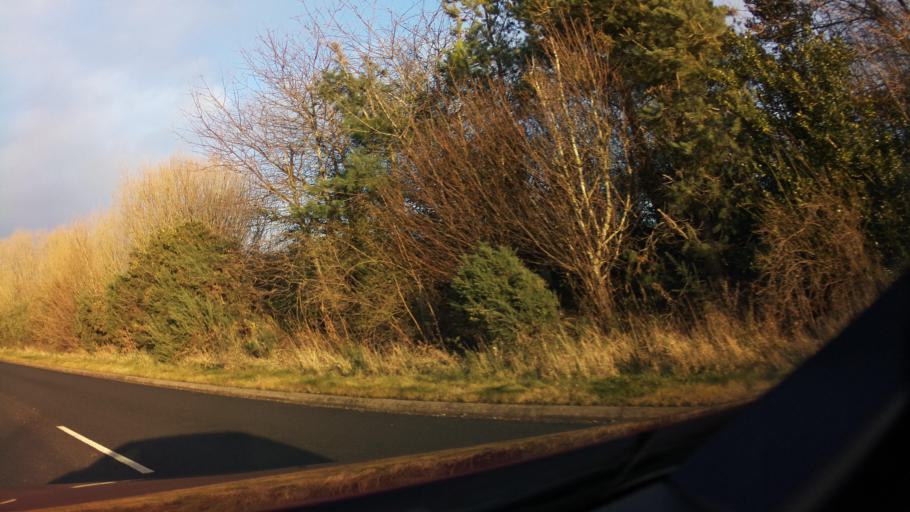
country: GB
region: Scotland
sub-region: Fife
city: Tayport
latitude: 56.4916
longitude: -2.8042
